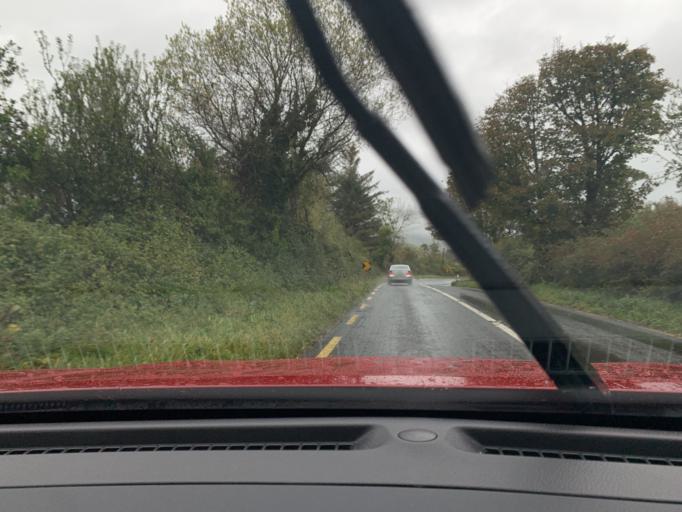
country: IE
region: Connaught
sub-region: Sligo
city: Sligo
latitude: 54.3194
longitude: -8.4302
